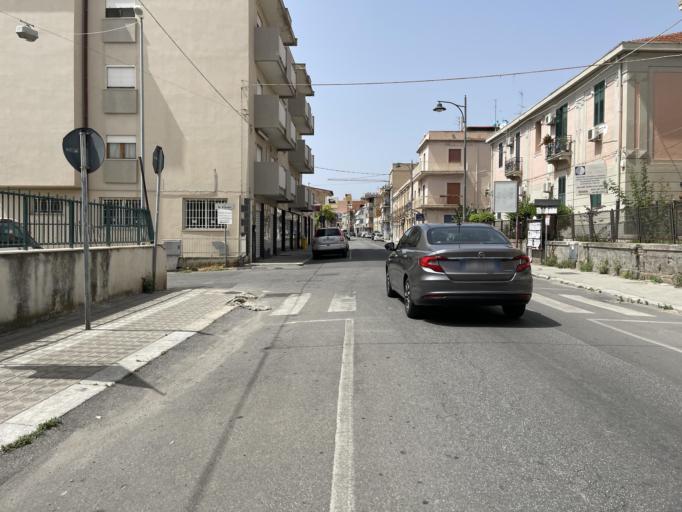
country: IT
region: Calabria
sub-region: Provincia di Reggio Calabria
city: Reggio Calabria
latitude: 38.0984
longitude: 15.6430
